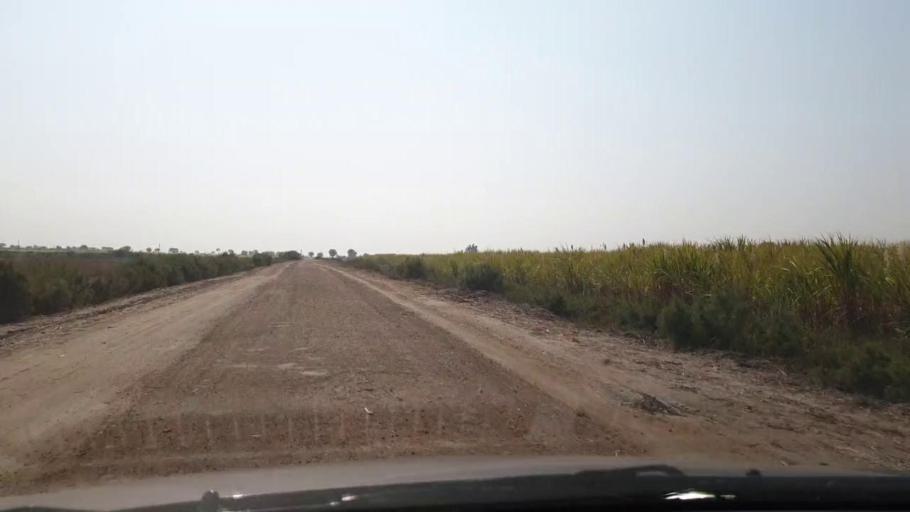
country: PK
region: Sindh
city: Jhol
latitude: 25.8666
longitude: 68.9980
